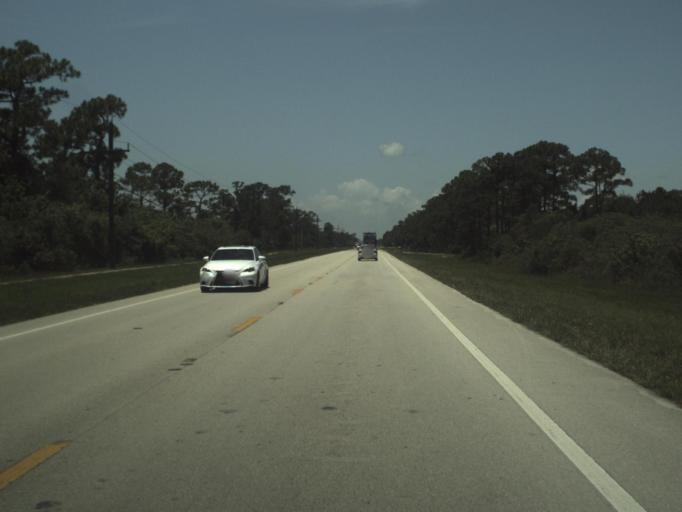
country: US
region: Florida
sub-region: Martin County
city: Palm City
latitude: 27.1618
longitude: -80.3610
